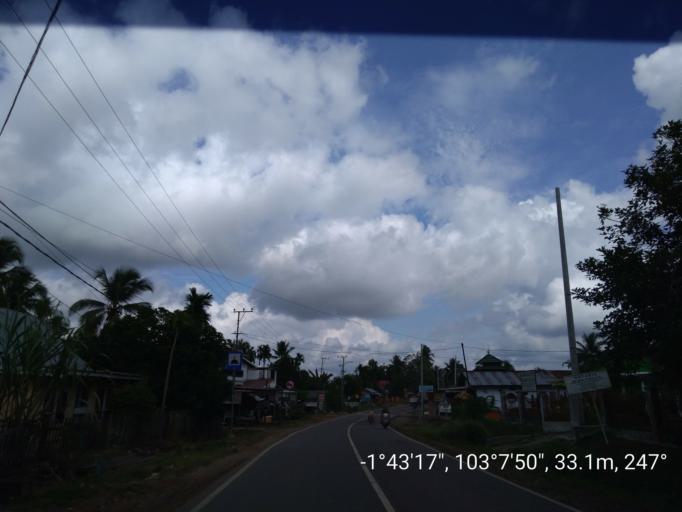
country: ID
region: Jambi
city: Muara Tembesi
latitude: -1.7214
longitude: 103.1307
